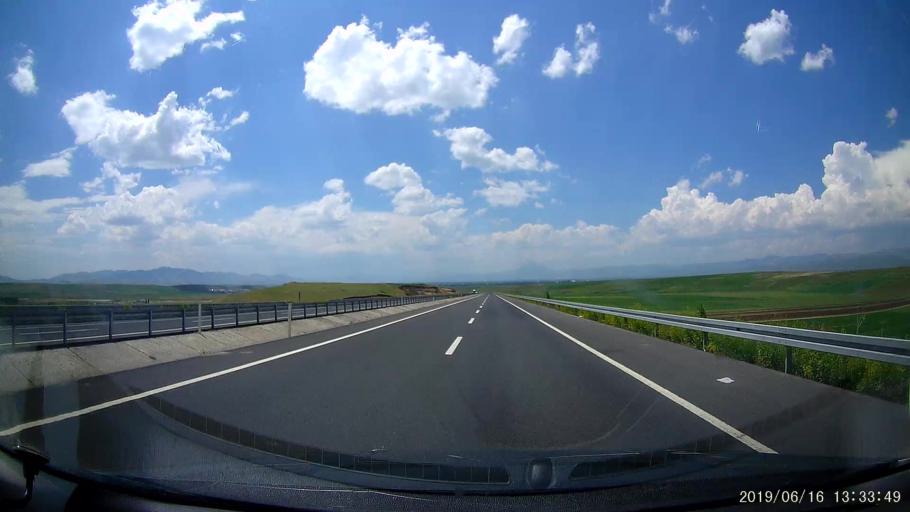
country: TR
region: Agri
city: Agri
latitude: 39.7089
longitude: 43.1440
